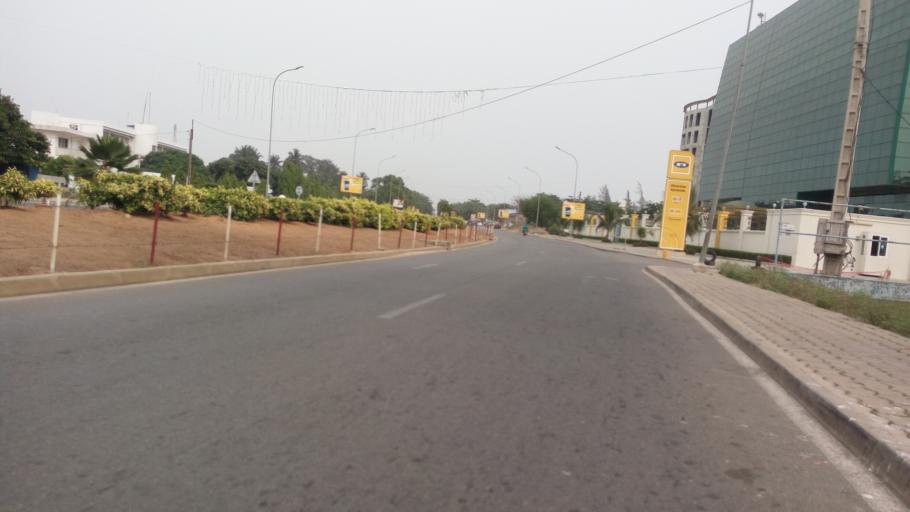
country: BJ
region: Littoral
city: Cotonou
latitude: 6.3492
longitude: 2.3975
